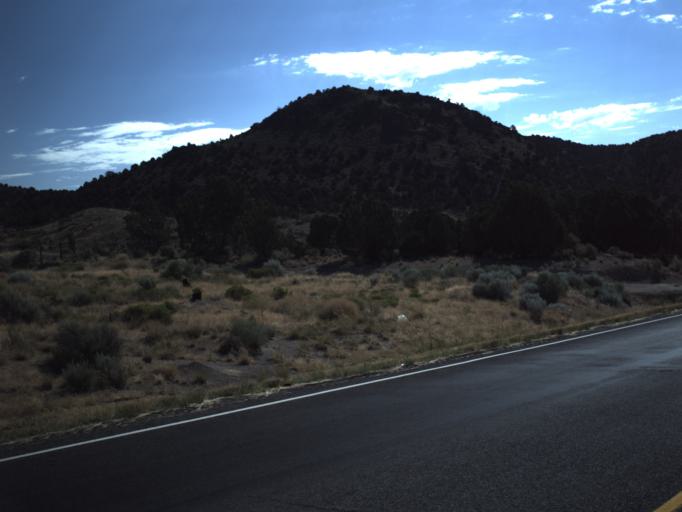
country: US
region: Utah
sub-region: Utah County
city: Genola
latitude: 39.9640
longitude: -112.0450
